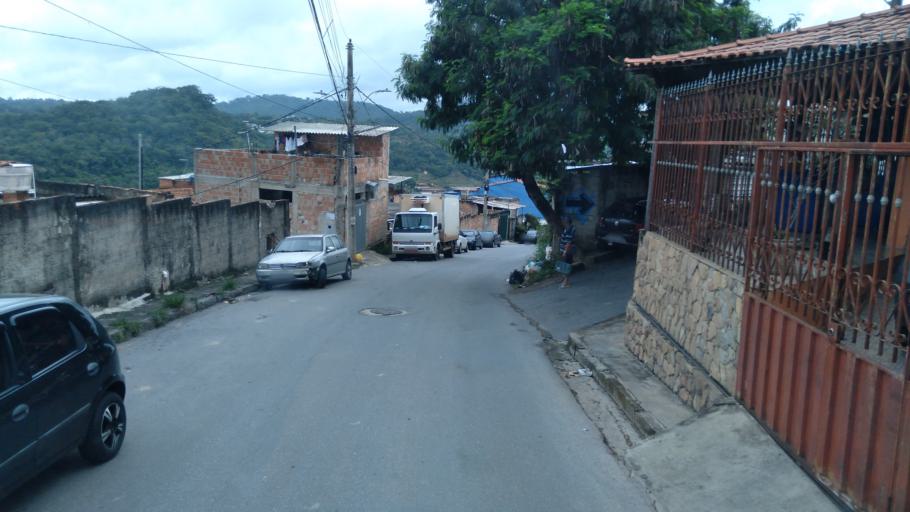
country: BR
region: Minas Gerais
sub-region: Santa Luzia
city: Santa Luzia
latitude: -19.8293
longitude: -43.8689
